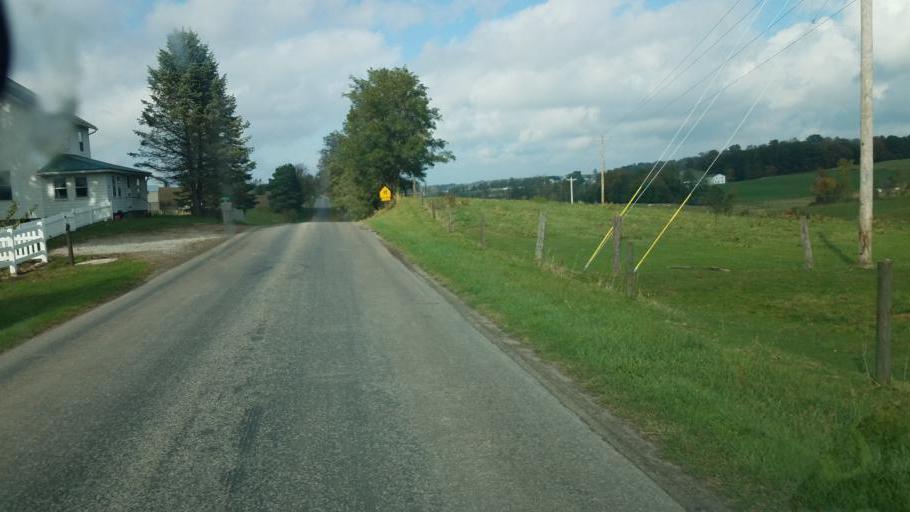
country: US
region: Ohio
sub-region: Wayne County
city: Apple Creek
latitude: 40.6472
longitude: -81.8613
